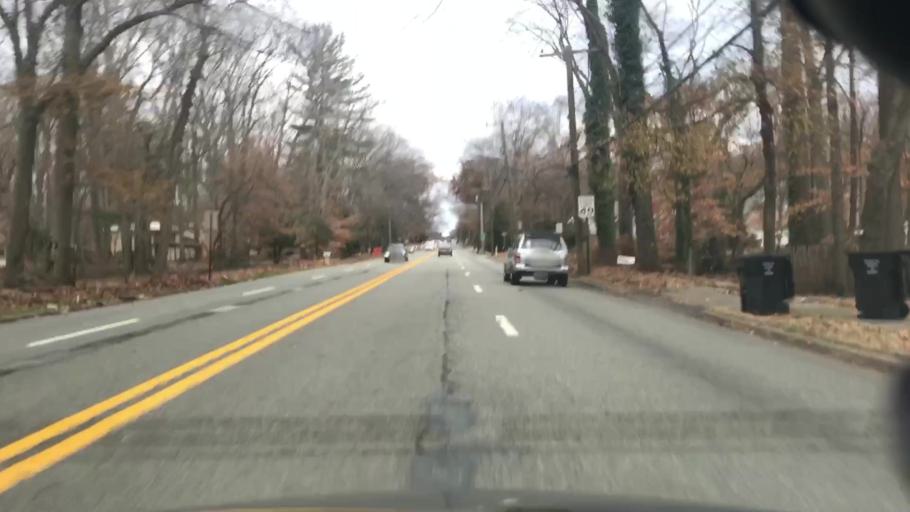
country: US
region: New Jersey
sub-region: Bergen County
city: River Edge
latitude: 40.9292
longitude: -74.0513
